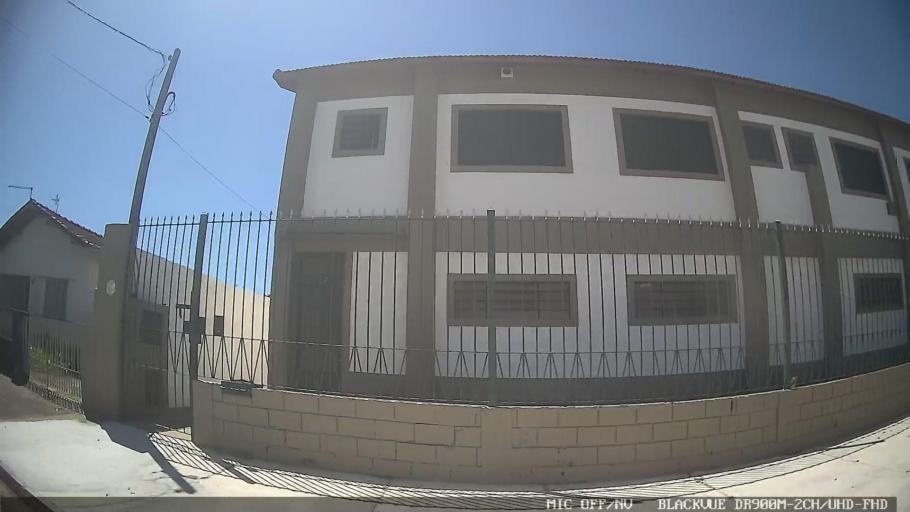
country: BR
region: Sao Paulo
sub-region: Atibaia
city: Atibaia
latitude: -23.1119
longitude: -46.5654
